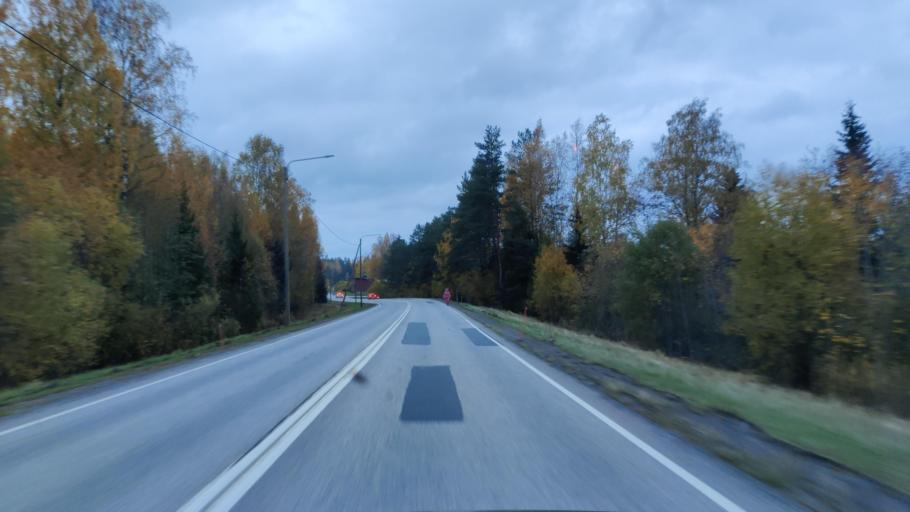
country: FI
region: Uusimaa
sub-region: Helsinki
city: Vihti
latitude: 60.3419
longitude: 24.1957
